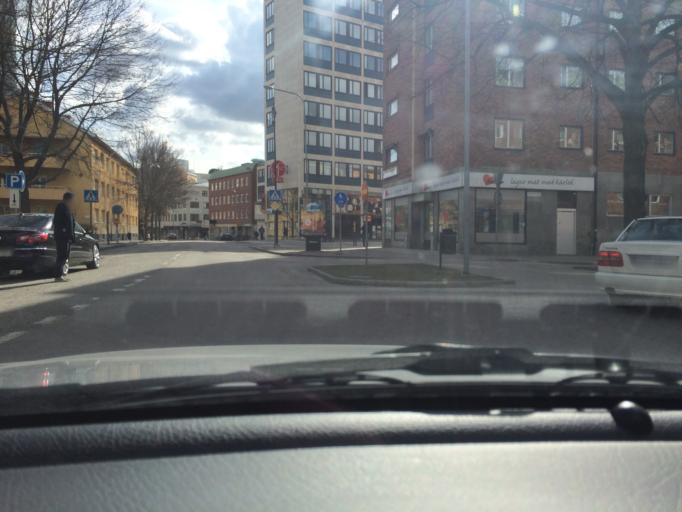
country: SE
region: Vaestmanland
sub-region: Vasteras
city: Vasteras
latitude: 59.6127
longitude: 16.5485
